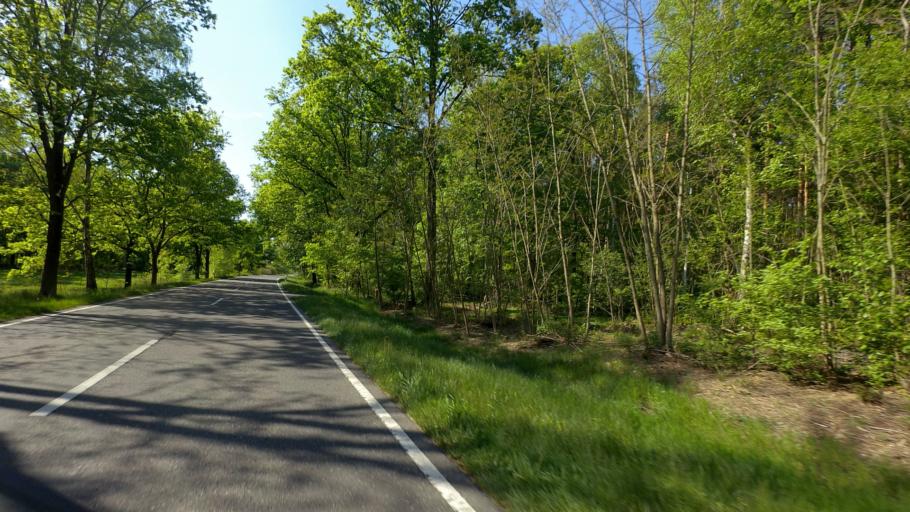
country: DE
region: Brandenburg
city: Schlepzig
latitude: 52.0684
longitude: 13.9042
